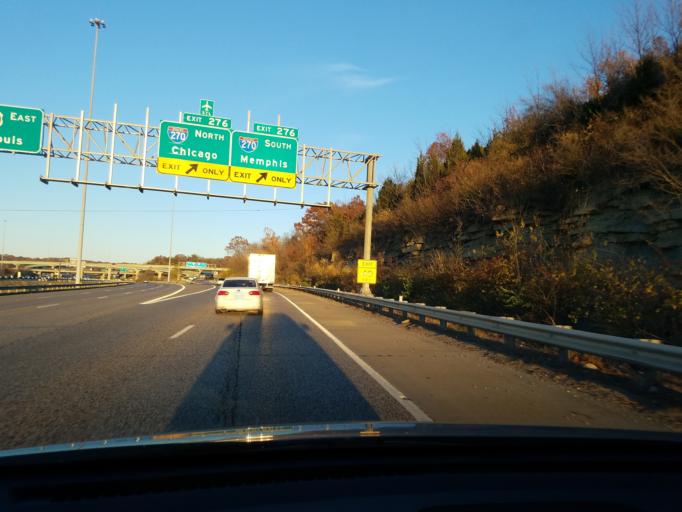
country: US
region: Missouri
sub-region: Saint Louis County
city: Sunset Hills
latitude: 38.5441
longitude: -90.4322
